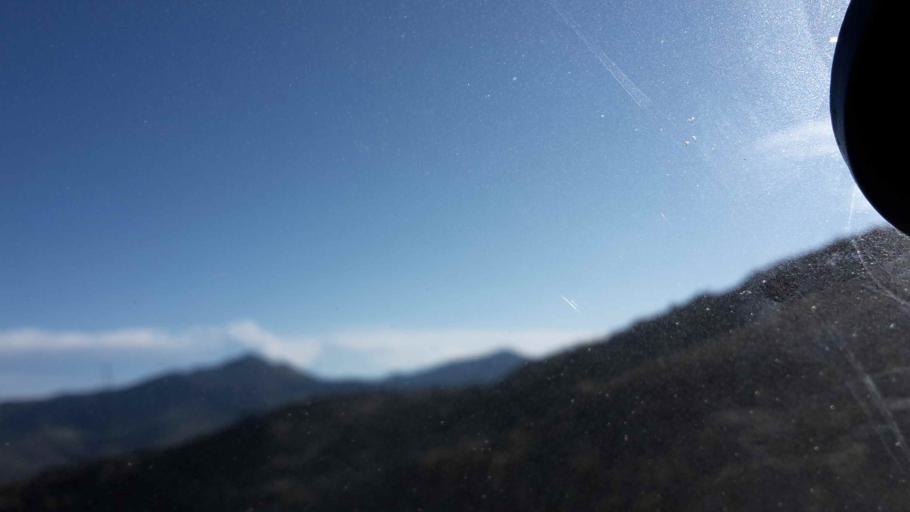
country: BO
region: Cochabamba
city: Arani
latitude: -17.7354
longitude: -65.6218
